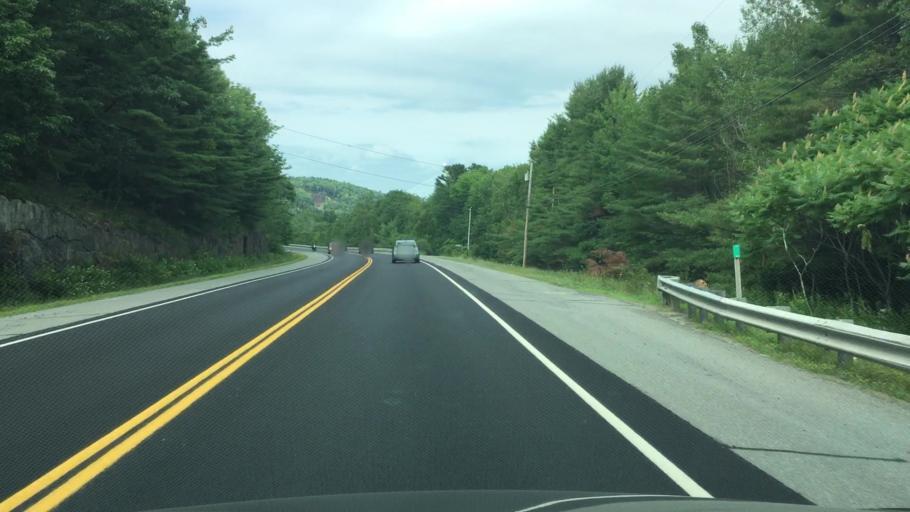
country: US
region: Maine
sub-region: Hancock County
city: Bucksport
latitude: 44.5445
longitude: -68.8093
